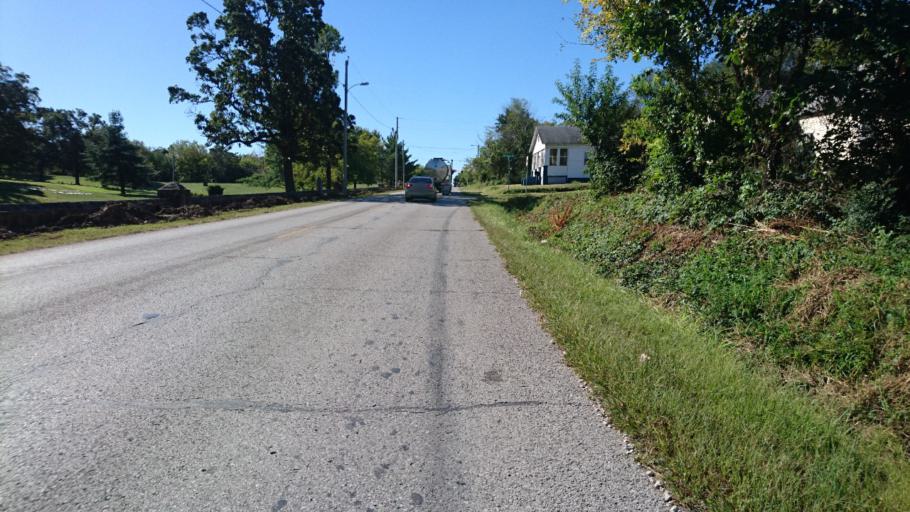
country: US
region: Missouri
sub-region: Jasper County
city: Joplin
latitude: 37.0936
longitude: -94.4947
